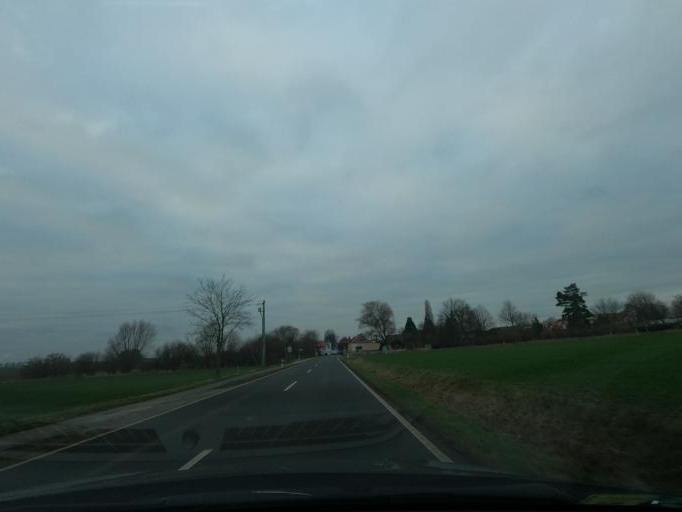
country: DE
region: Lower Saxony
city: Borssum
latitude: 52.0688
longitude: 10.5956
